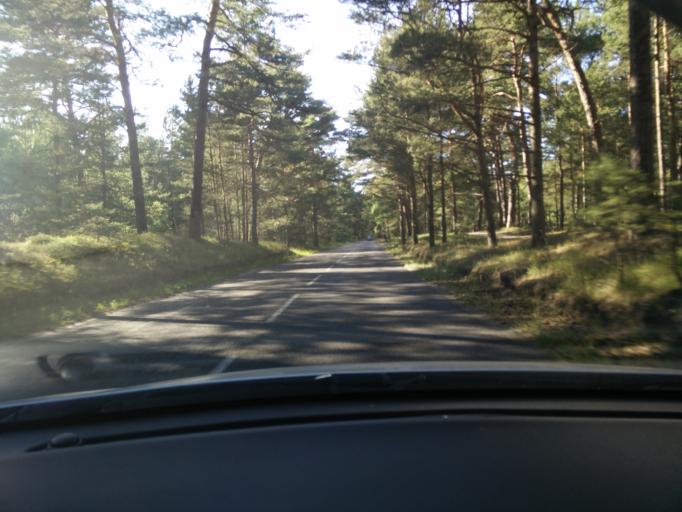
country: PL
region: Pomeranian Voivodeship
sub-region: Powiat pucki
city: Hel
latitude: 54.6374
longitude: 18.7771
